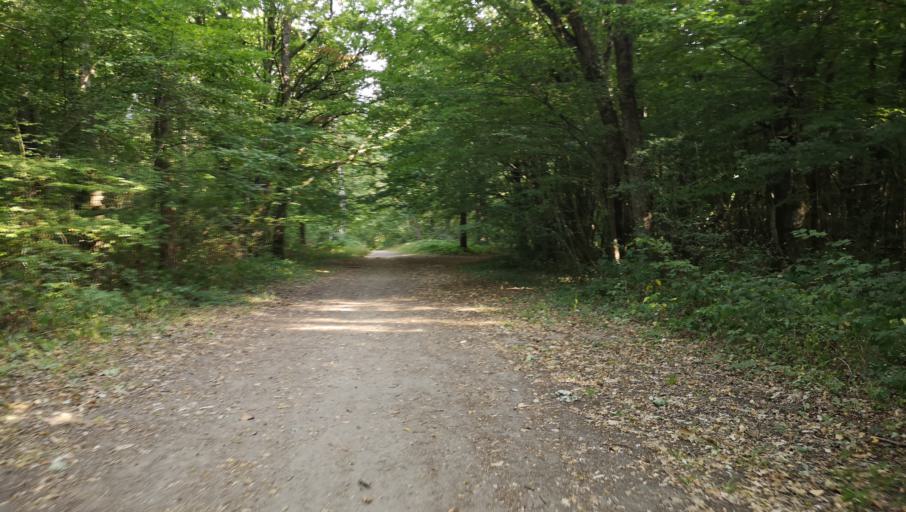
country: FR
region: Centre
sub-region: Departement du Loiret
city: Boigny-sur-Bionne
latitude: 47.9405
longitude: 1.9943
